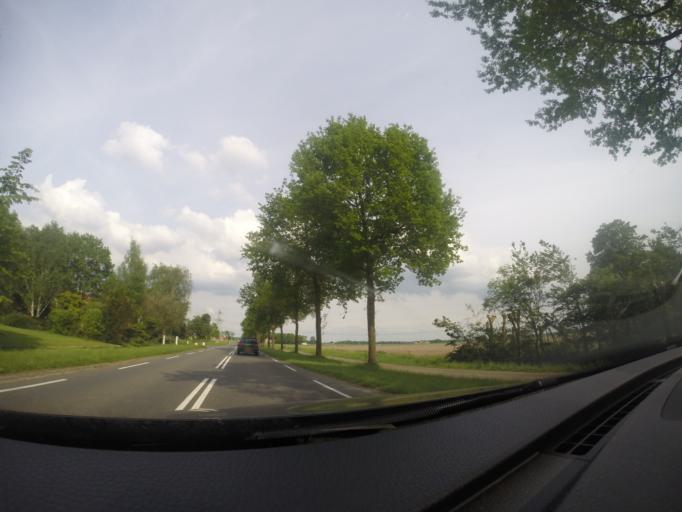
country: NL
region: Flevoland
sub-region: Gemeente Noordoostpolder
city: Ens
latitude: 52.6365
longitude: 5.8061
